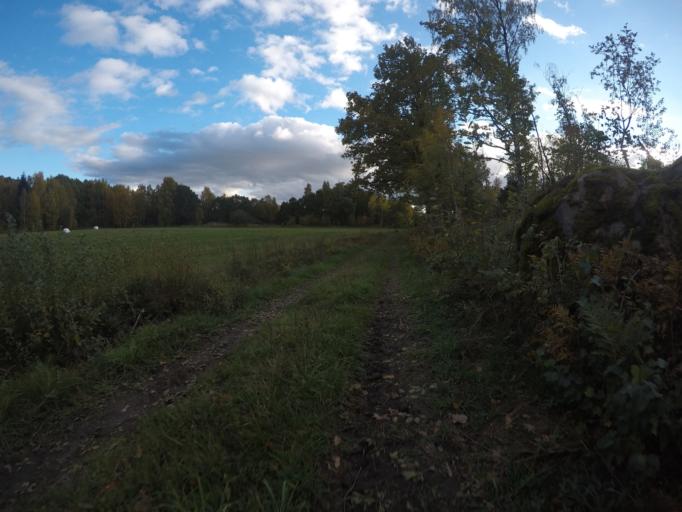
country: SE
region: Vaestmanland
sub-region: Arboga Kommun
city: Tyringe
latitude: 59.2951
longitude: 15.9975
